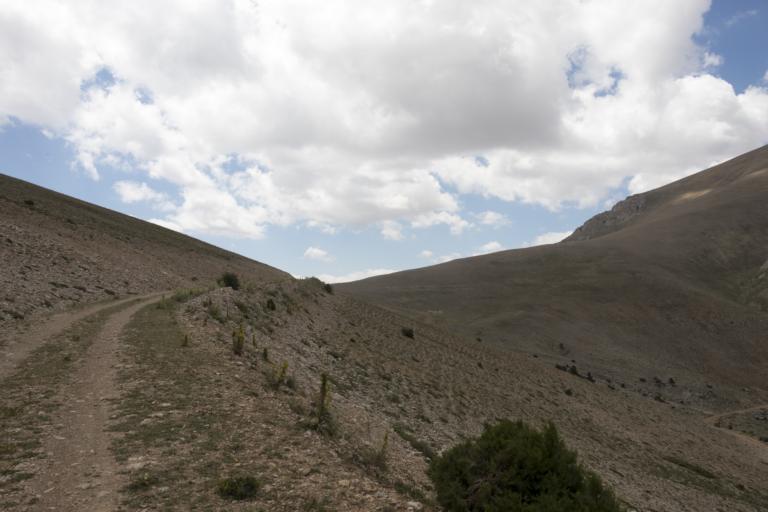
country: TR
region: Kayseri
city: Toklar
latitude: 38.3170
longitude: 36.0960
